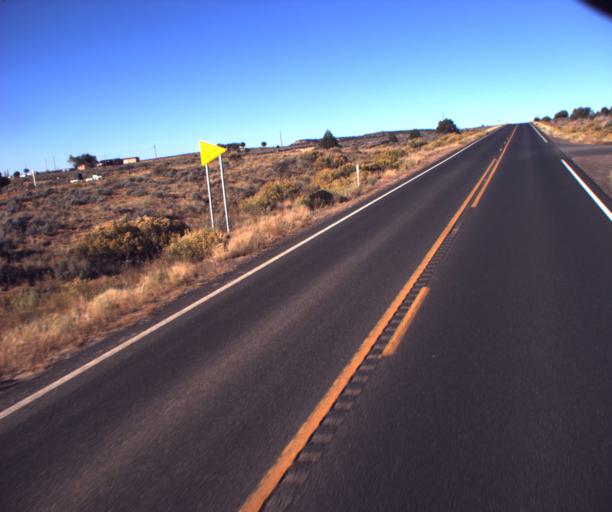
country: US
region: Arizona
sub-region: Apache County
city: Ganado
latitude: 35.7606
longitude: -109.7584
